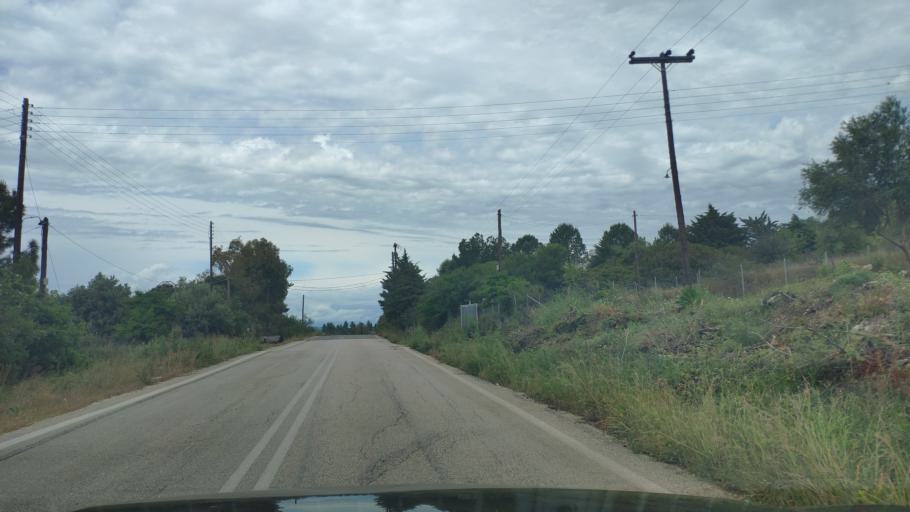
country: GR
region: West Greece
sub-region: Nomos Aitolias kai Akarnanias
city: Palairos
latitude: 38.7632
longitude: 20.8819
